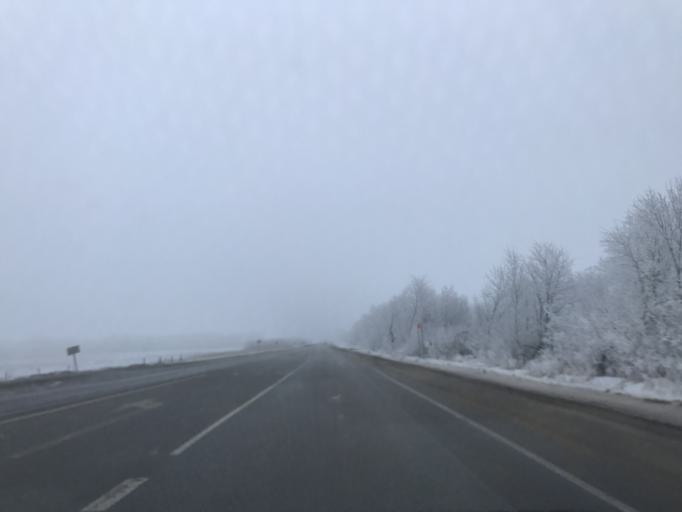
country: RU
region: Rostov
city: Grushevskaya
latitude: 47.3787
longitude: 39.8791
